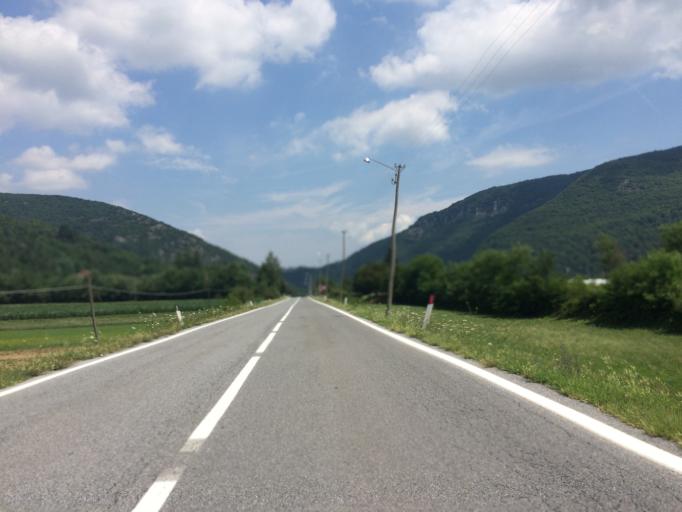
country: IT
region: Piedmont
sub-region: Provincia di Cuneo
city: Priola
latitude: 44.2609
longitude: 8.0244
